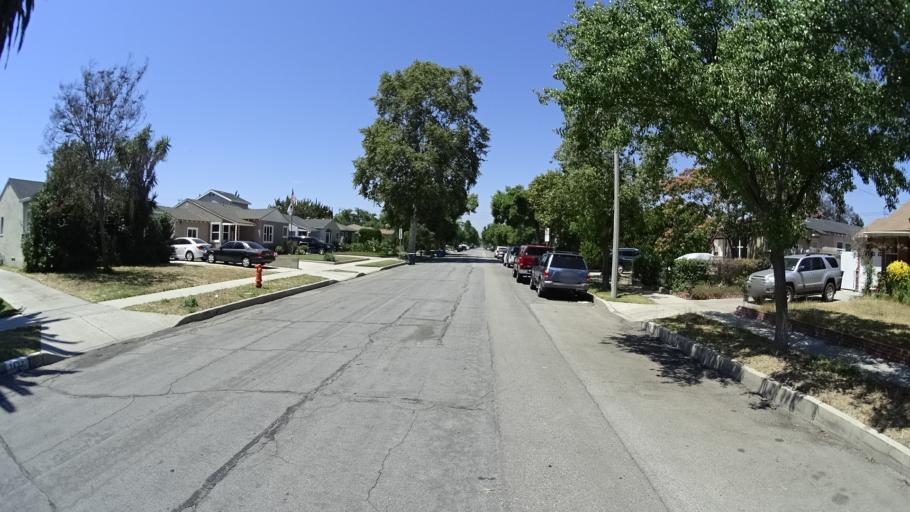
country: US
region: California
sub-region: Los Angeles County
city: North Hollywood
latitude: 34.1740
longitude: -118.3568
